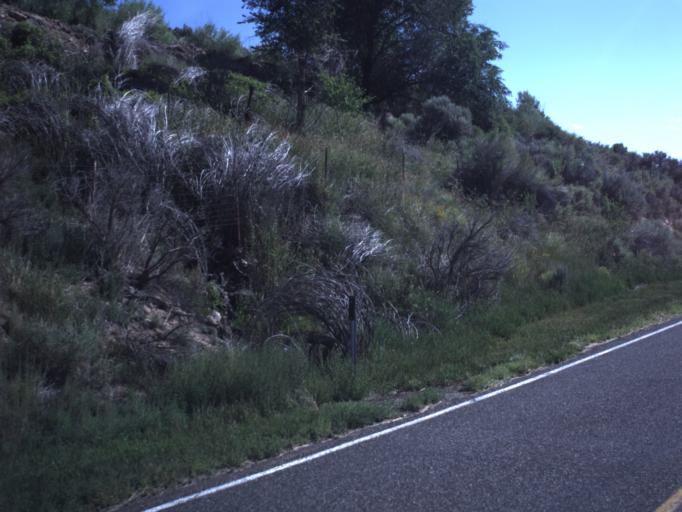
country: US
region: Utah
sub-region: Wayne County
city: Loa
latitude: 38.4603
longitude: -111.6122
